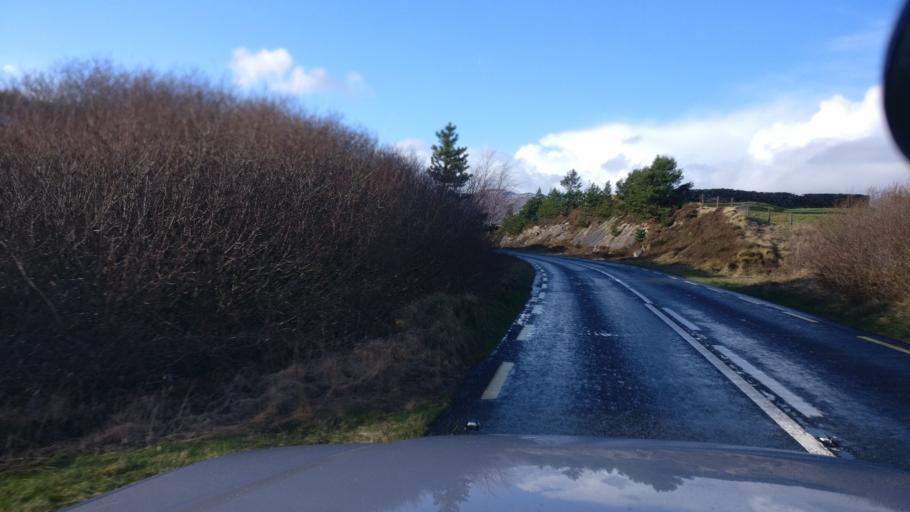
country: IE
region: Connaught
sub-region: County Galway
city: Oughterard
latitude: 53.4563
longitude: -9.6617
